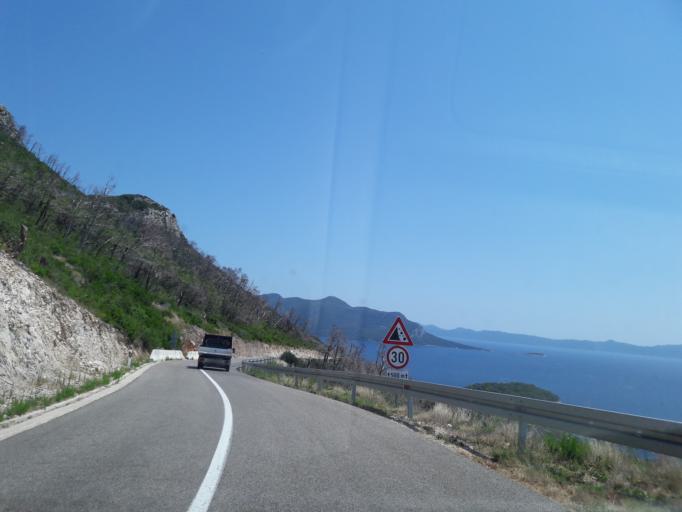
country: HR
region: Dubrovacko-Neretvanska
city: Komin
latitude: 42.9229
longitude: 17.4056
